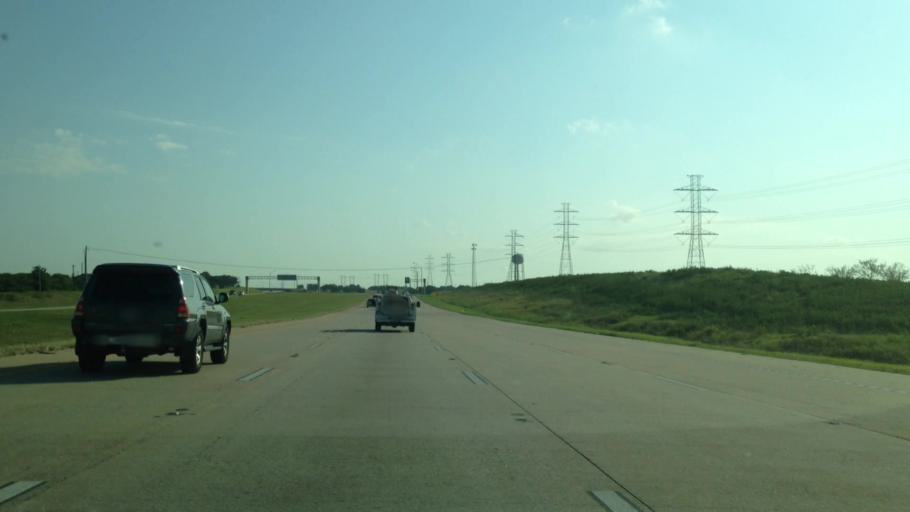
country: US
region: Texas
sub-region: Travis County
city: Hornsby Bend
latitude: 30.2758
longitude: -97.5865
